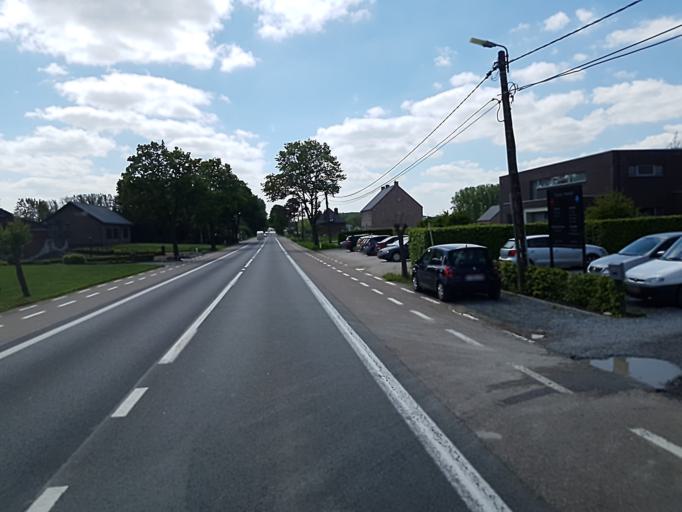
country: BE
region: Flanders
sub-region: Provincie Vlaams-Brabant
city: Glabbeek-Zuurbemde
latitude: 50.8615
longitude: 4.9555
